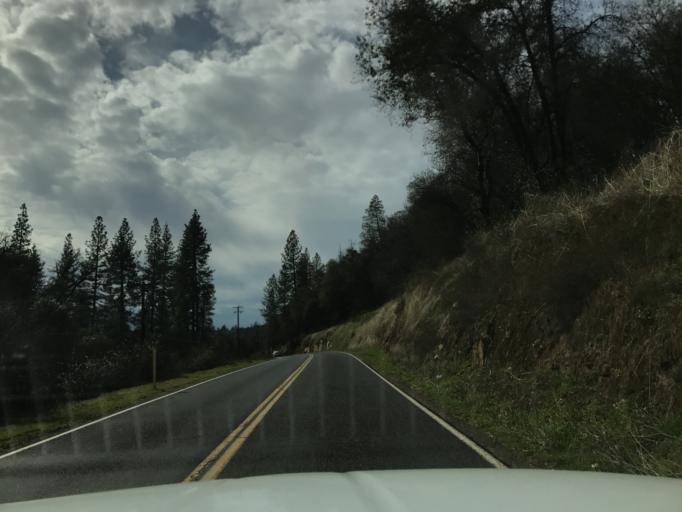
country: US
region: California
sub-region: Calaveras County
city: Mountain Ranch
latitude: 38.2316
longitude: -120.5364
